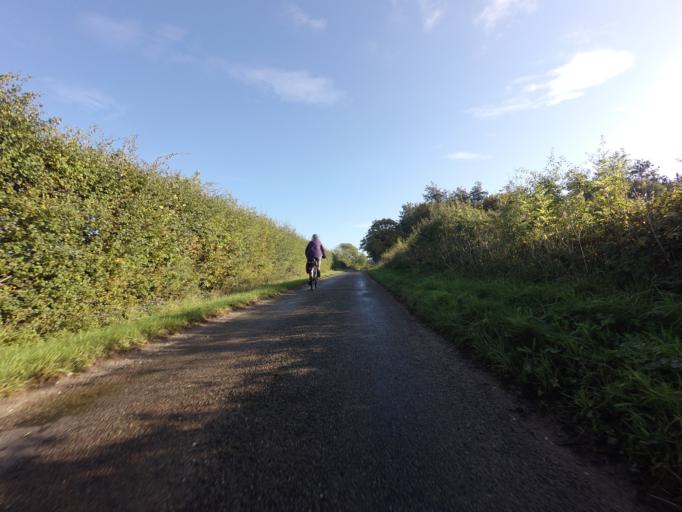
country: GB
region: England
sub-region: Norfolk
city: Dersingham
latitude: 52.8298
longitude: 0.5629
